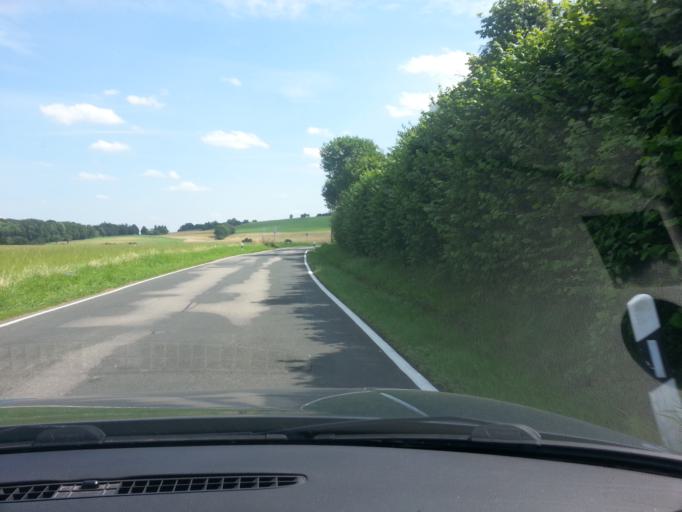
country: DE
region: Saarland
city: Blieskastel
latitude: 49.2006
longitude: 7.2820
